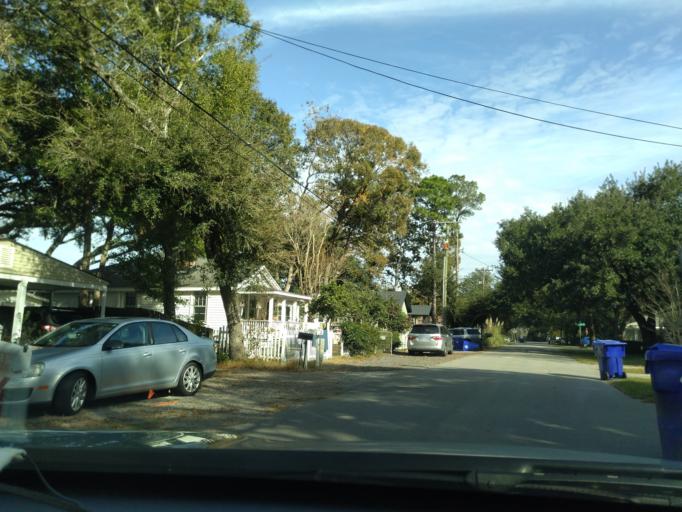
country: US
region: South Carolina
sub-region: Charleston County
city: North Charleston
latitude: 32.8027
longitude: -80.0103
